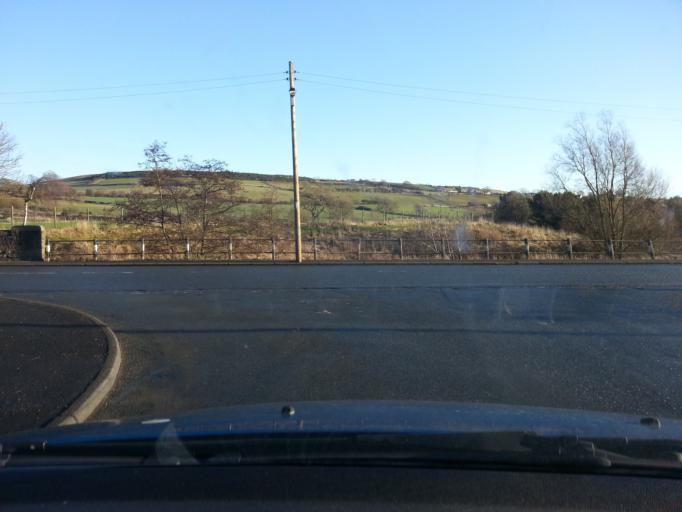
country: GB
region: England
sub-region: County Durham
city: Crook
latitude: 54.7217
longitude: -1.7506
